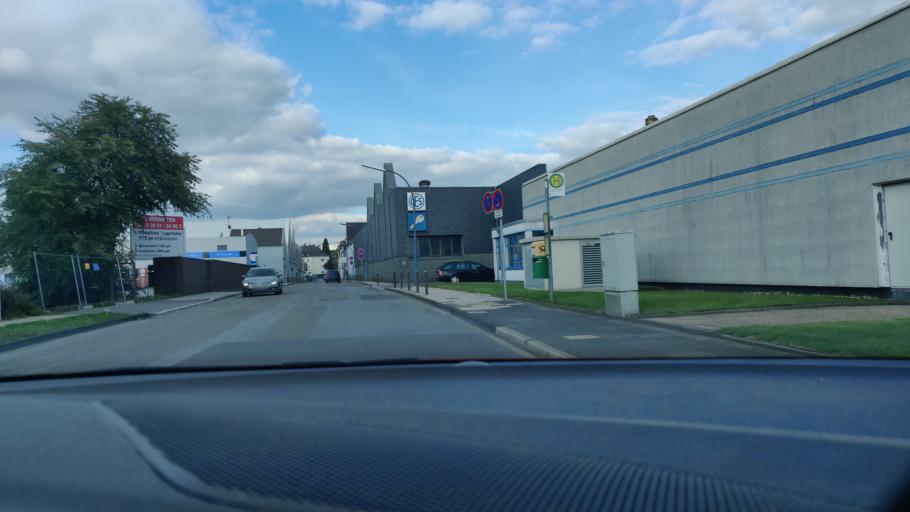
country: DE
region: North Rhine-Westphalia
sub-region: Regierungsbezirk Dusseldorf
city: Velbert
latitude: 51.3272
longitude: 7.0485
